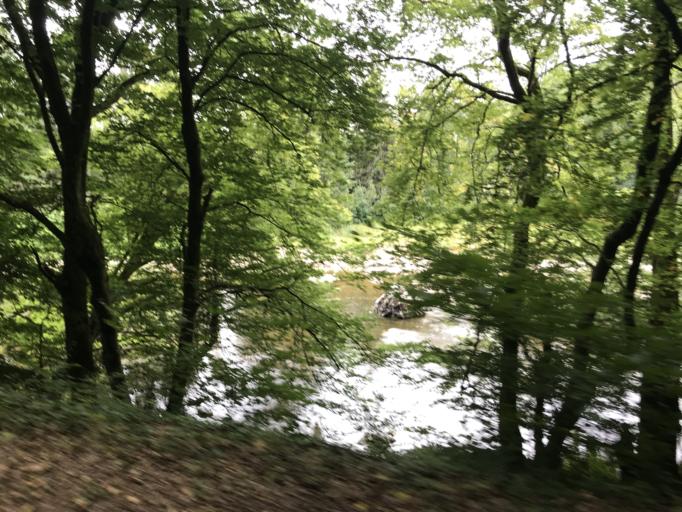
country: FR
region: Champagne-Ardenne
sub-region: Departement des Ardennes
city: Thilay
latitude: 49.8768
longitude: 4.7838
